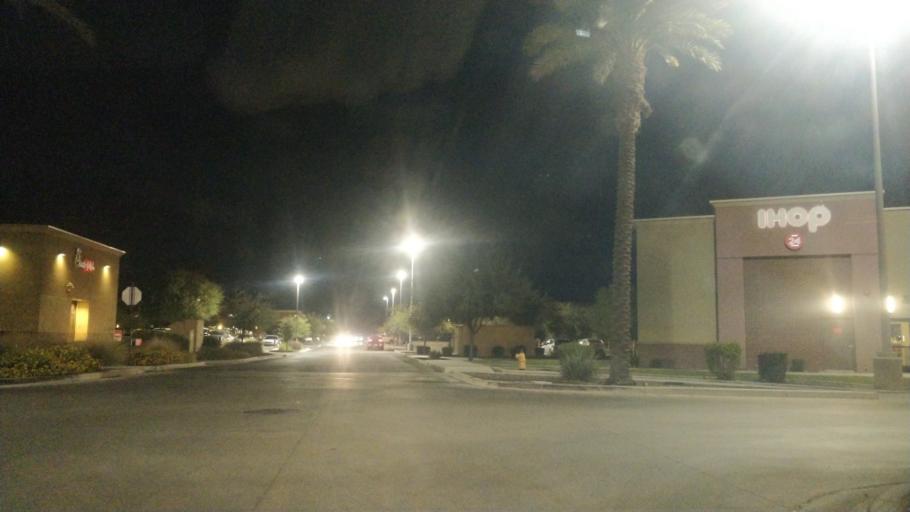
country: US
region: Arizona
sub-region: Maricopa County
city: Sun Lakes
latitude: 33.2493
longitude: -111.8402
